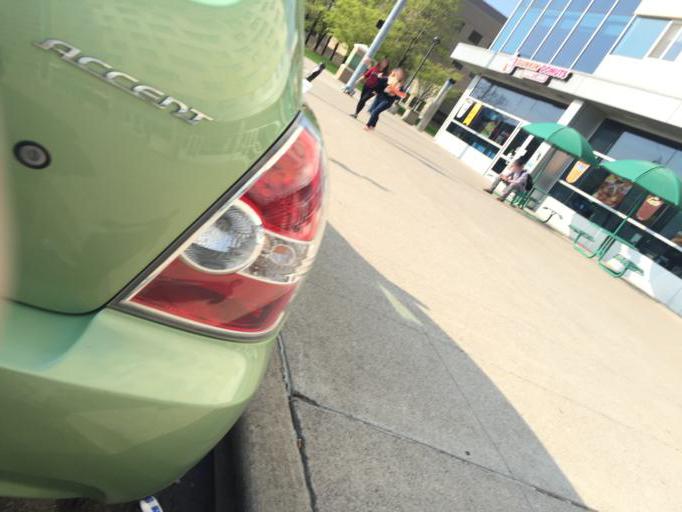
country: US
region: Michigan
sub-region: Wayne County
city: Detroit
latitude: 42.3577
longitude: -83.0729
